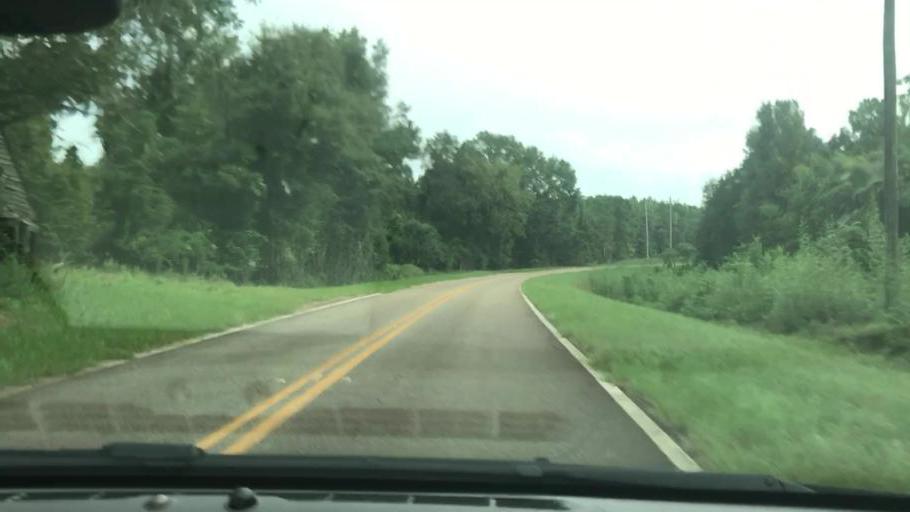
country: US
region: Georgia
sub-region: Stewart County
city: Lumpkin
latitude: 32.0471
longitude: -84.9058
